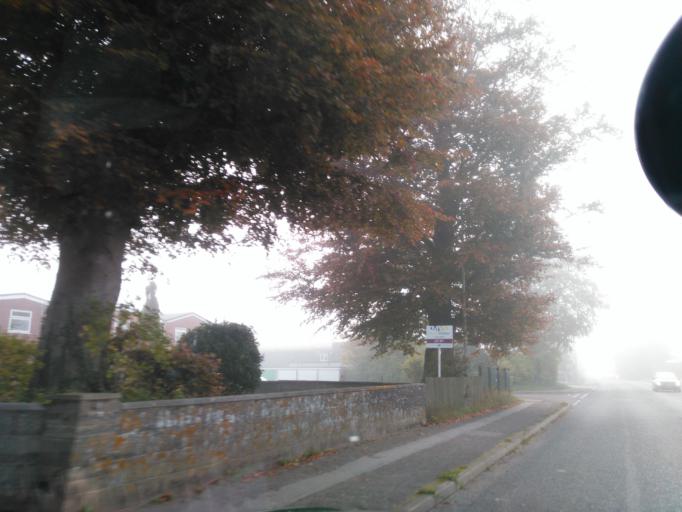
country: GB
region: England
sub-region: Wiltshire
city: Devizes
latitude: 51.3450
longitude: -1.9791
